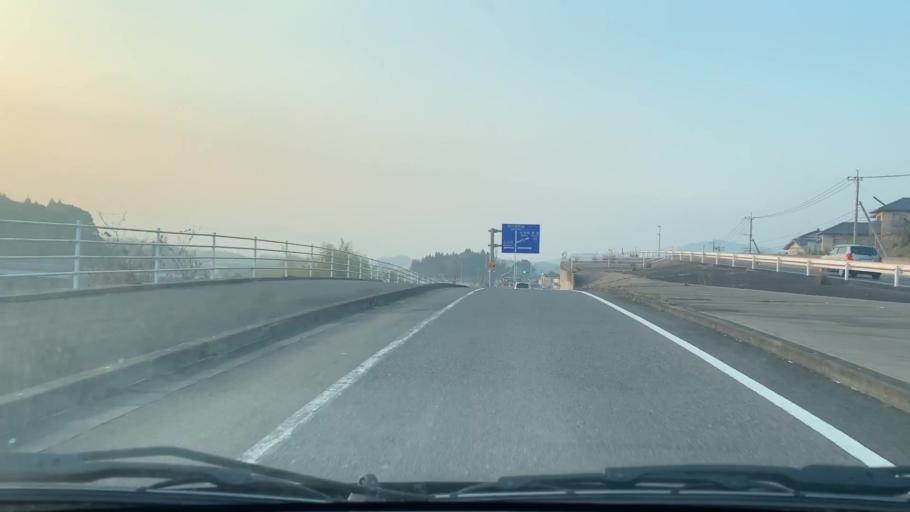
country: JP
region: Saga Prefecture
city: Imaricho-ko
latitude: 33.2633
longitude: 129.9091
